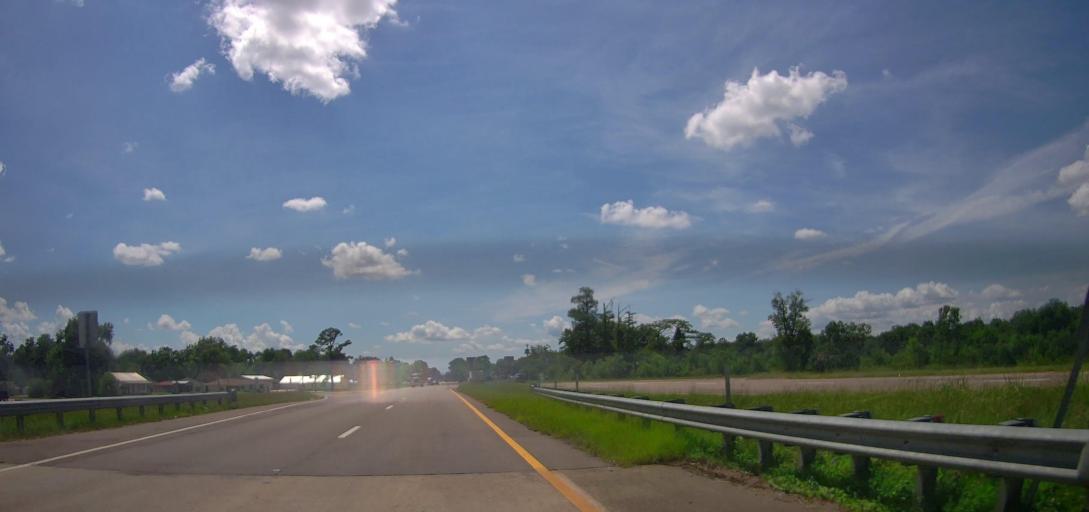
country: US
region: Mississippi
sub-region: Monroe County
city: Aberdeen
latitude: 33.8154
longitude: -88.5388
